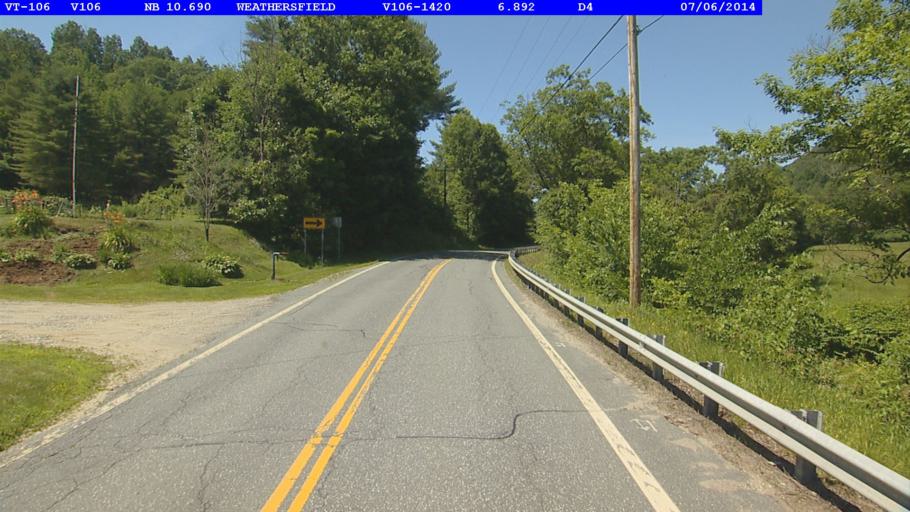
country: US
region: Vermont
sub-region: Windsor County
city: Springfield
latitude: 43.4342
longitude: -72.5284
